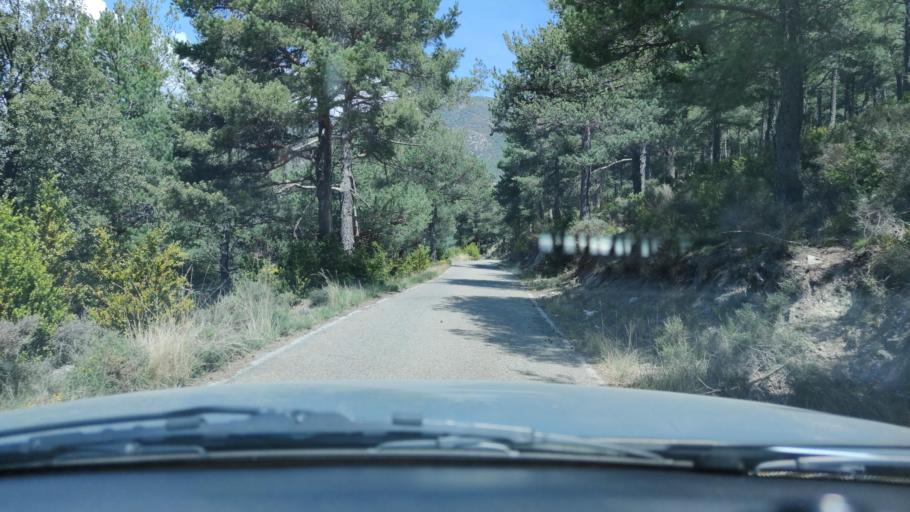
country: ES
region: Catalonia
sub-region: Provincia de Lleida
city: Sort
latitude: 42.3176
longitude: 1.1008
